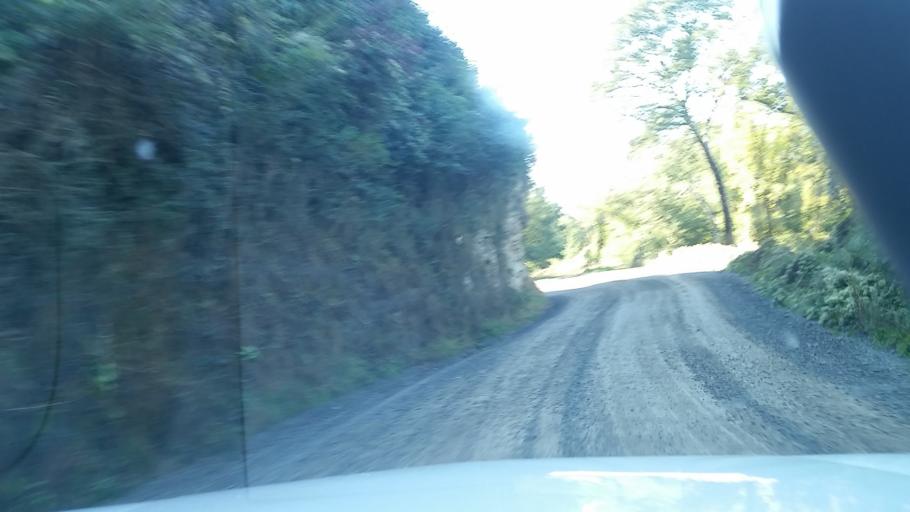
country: NZ
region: Marlborough
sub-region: Marlborough District
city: Blenheim
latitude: -41.4455
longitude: 173.8940
